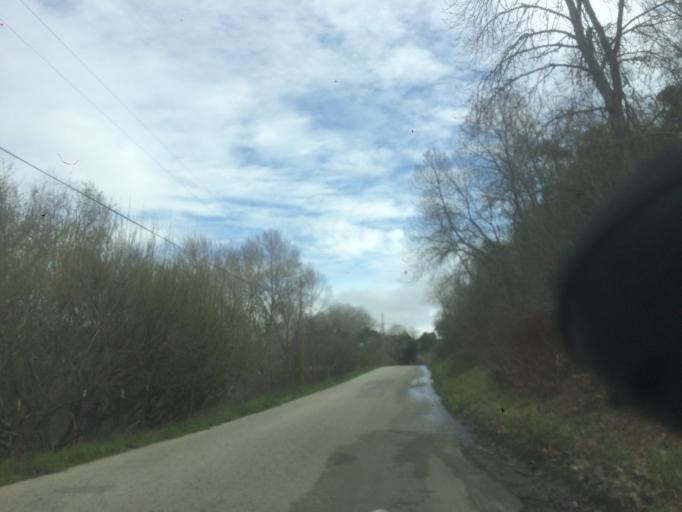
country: US
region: California
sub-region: San Luis Obispo County
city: Nipomo
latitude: 35.2033
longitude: -120.4268
